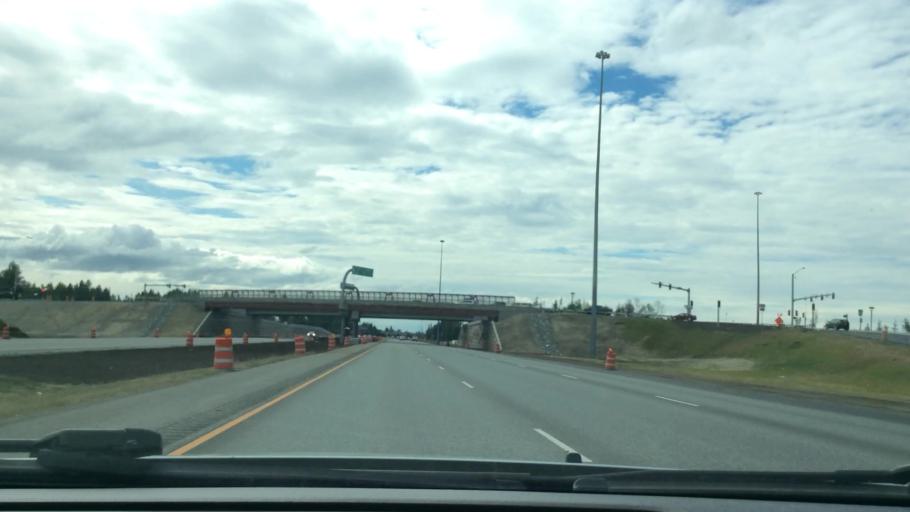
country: US
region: Alaska
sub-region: Anchorage Municipality
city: Elmendorf Air Force Base
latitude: 61.2281
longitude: -149.7297
